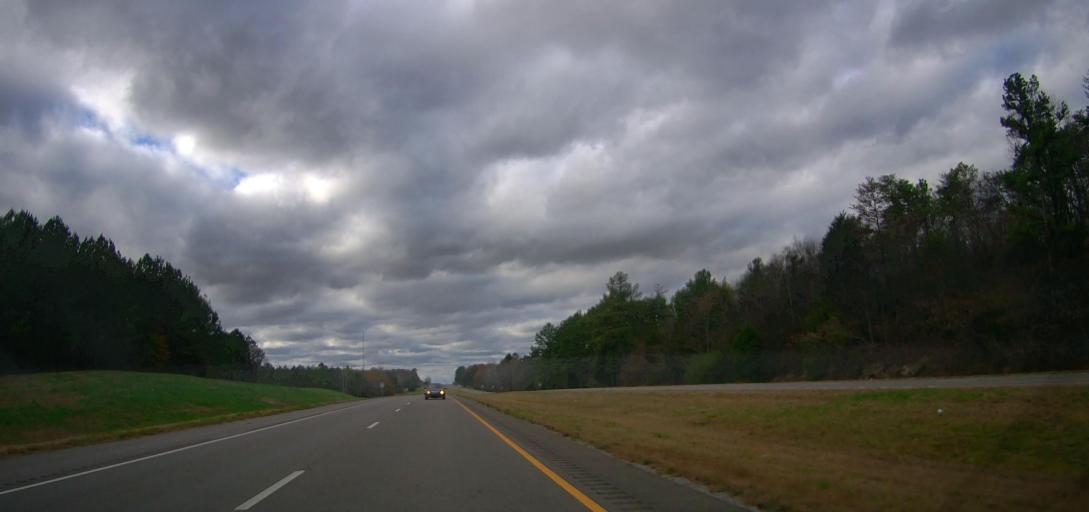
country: US
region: Alabama
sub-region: Morgan County
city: Danville
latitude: 34.3520
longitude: -87.0462
